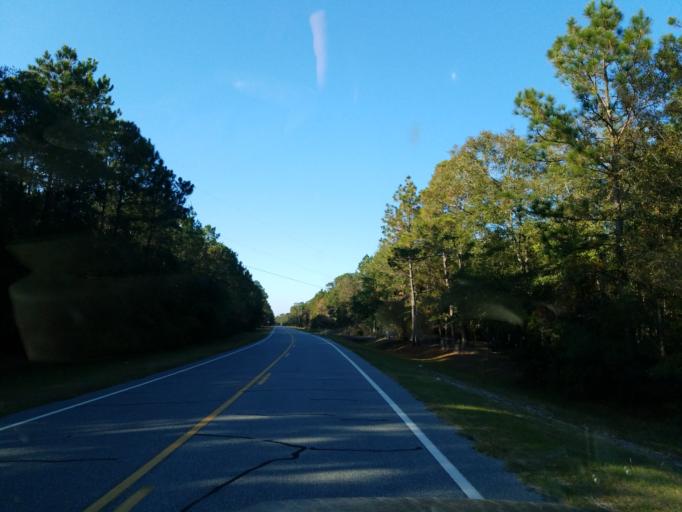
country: US
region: Georgia
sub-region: Lanier County
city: Lakeland
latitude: 30.8874
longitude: -83.0537
